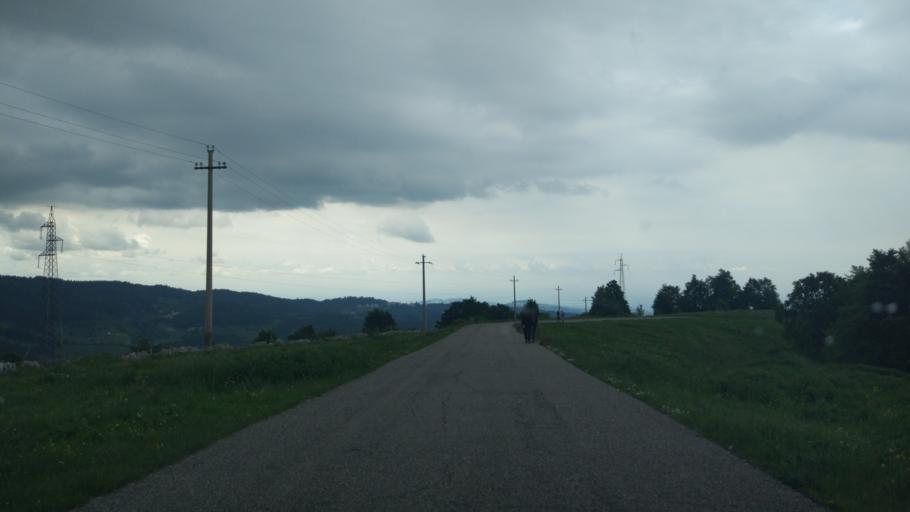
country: IT
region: Veneto
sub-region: Provincia di Verona
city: Erbezzo
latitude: 45.6598
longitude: 11.0011
